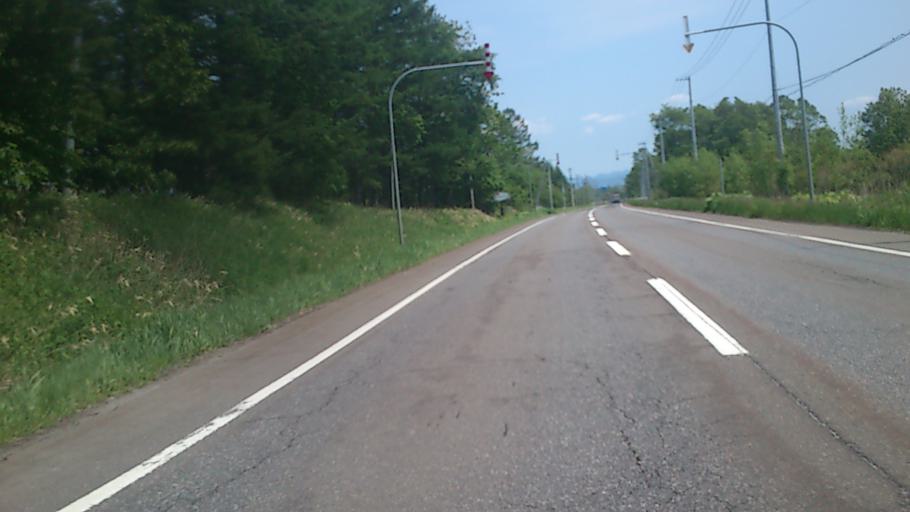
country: JP
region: Hokkaido
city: Otofuke
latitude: 43.2307
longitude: 143.5149
